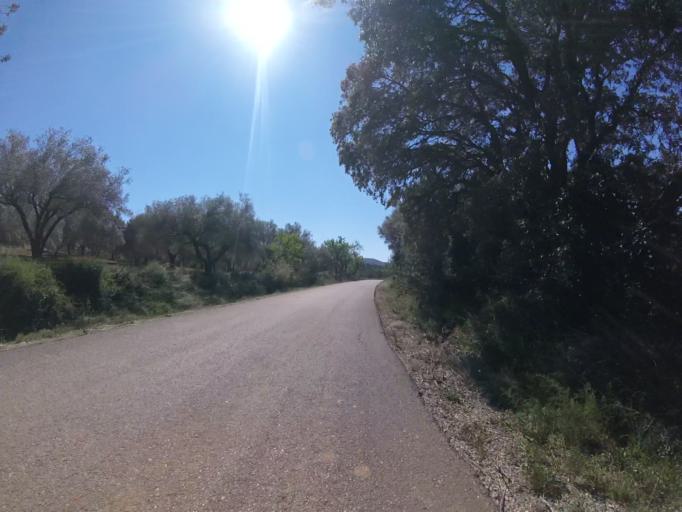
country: ES
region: Valencia
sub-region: Provincia de Castello
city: Cuevas de Vinroma
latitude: 40.3937
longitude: 0.1625
